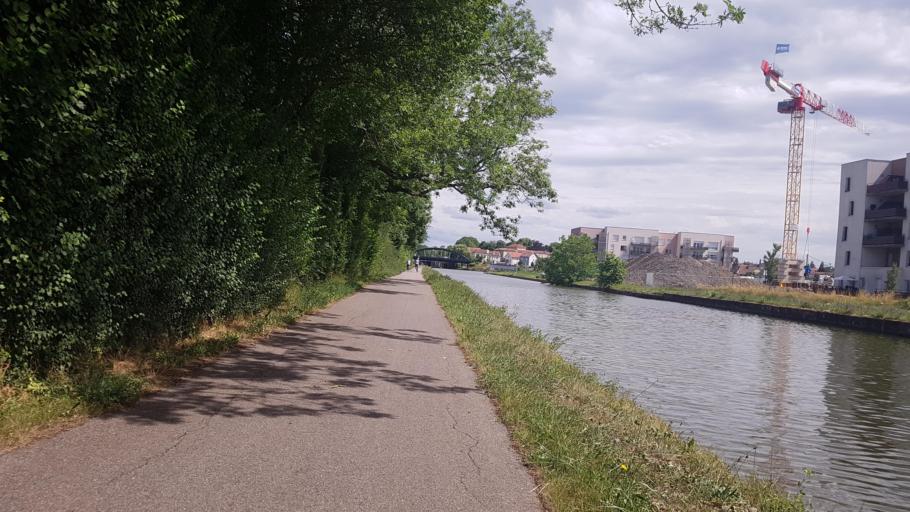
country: FR
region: Lorraine
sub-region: Departement de Meurthe-et-Moselle
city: Laneuveville-devant-Nancy
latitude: 48.6622
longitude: 6.2268
